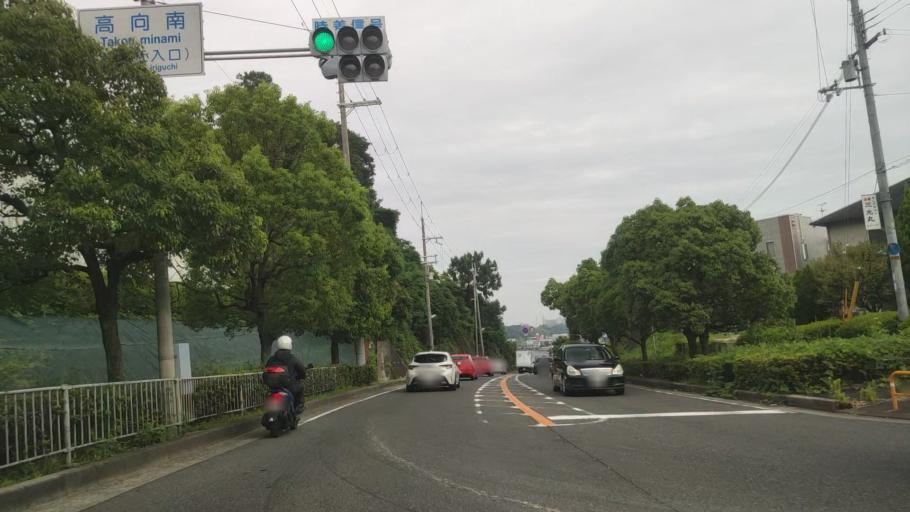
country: JP
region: Osaka
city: Tondabayashicho
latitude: 34.4357
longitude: 135.5580
